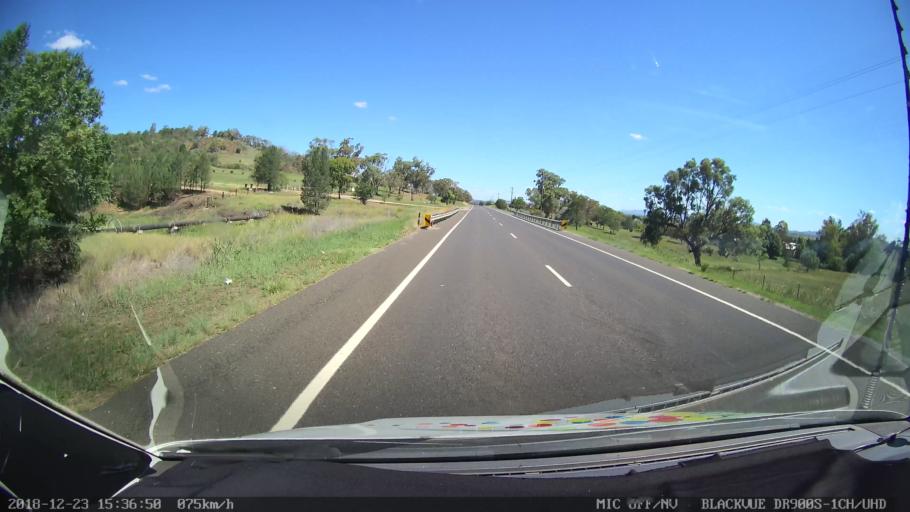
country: AU
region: New South Wales
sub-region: Tamworth Municipality
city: Tamworth
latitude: -31.0456
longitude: 150.8880
